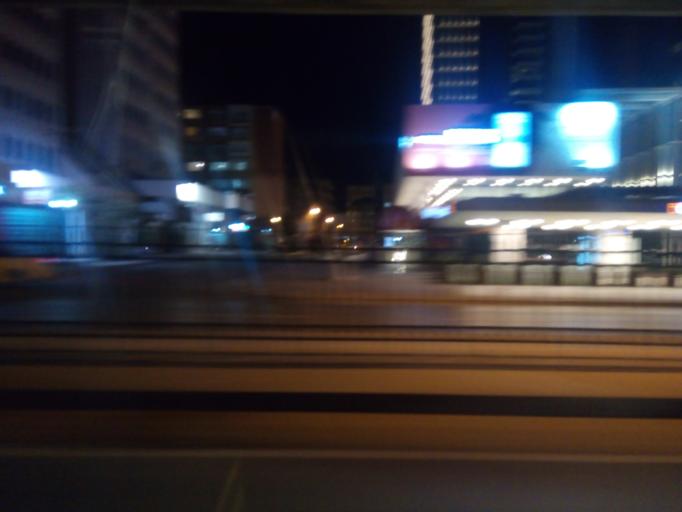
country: TR
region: Istanbul
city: Sisli
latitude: 41.0661
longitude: 29.0006
